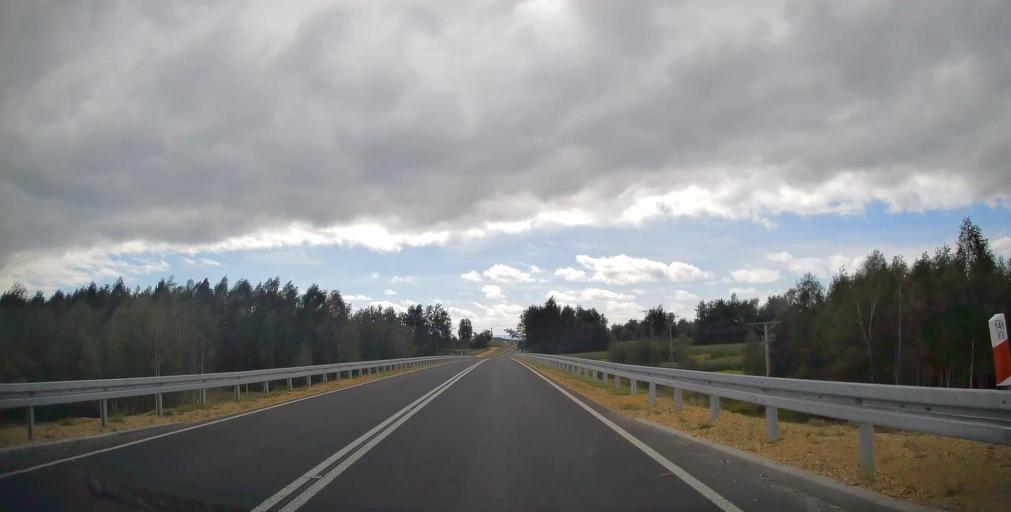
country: PL
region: Lesser Poland Voivodeship
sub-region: Powiat oswiecimski
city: Zator
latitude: 50.0029
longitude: 19.4226
